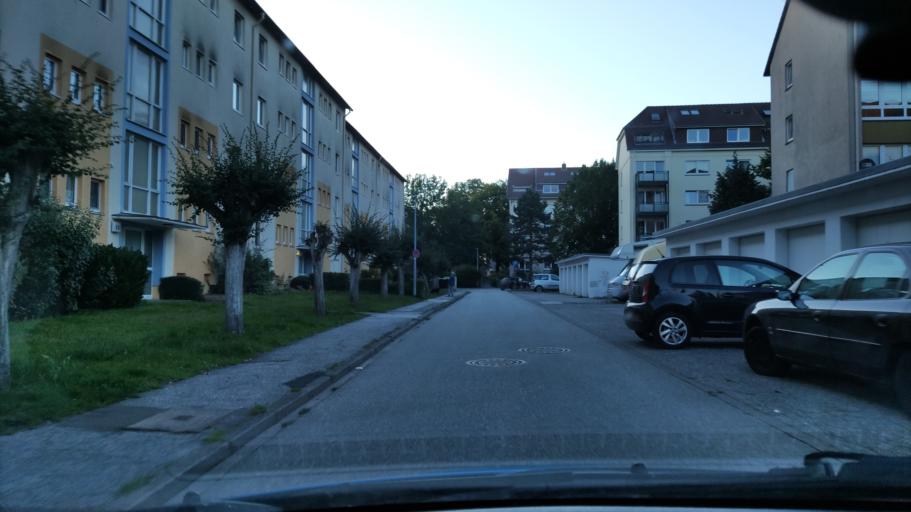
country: DE
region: Schleswig-Holstein
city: Wedel
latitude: 53.5687
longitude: 9.7127
